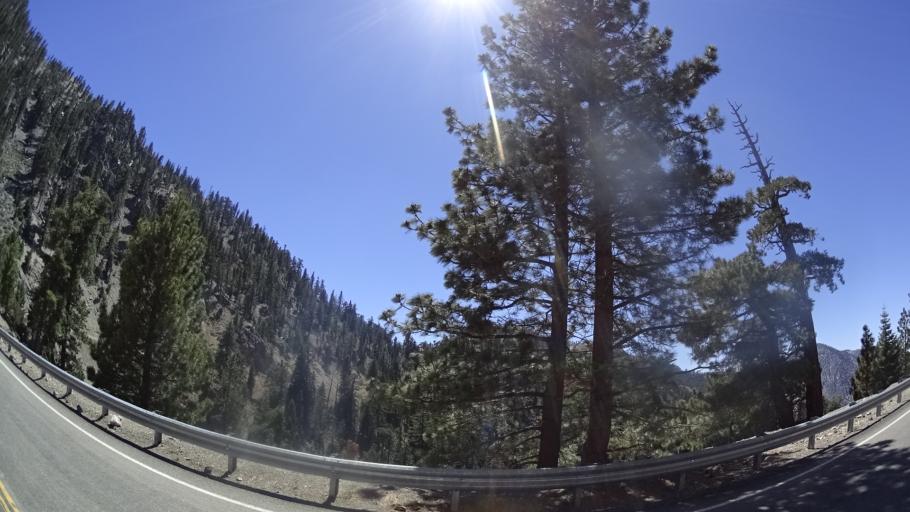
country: US
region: California
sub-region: San Bernardino County
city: Wrightwood
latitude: 34.3459
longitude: -117.8204
